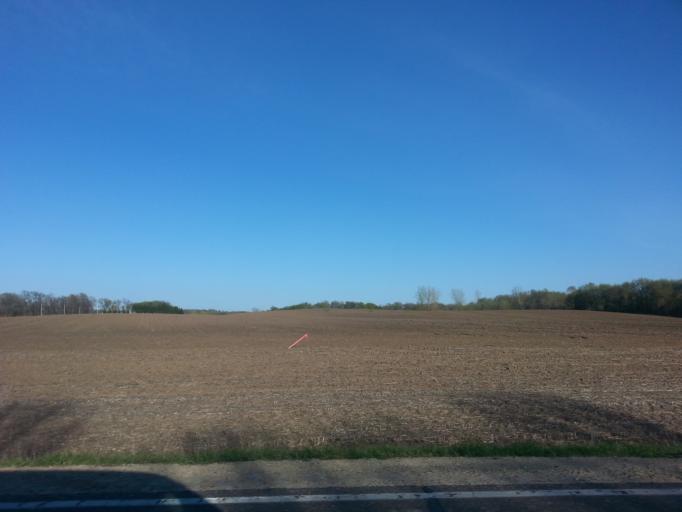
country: US
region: Minnesota
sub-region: Dakota County
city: Lakeville
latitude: 44.5927
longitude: -93.2679
